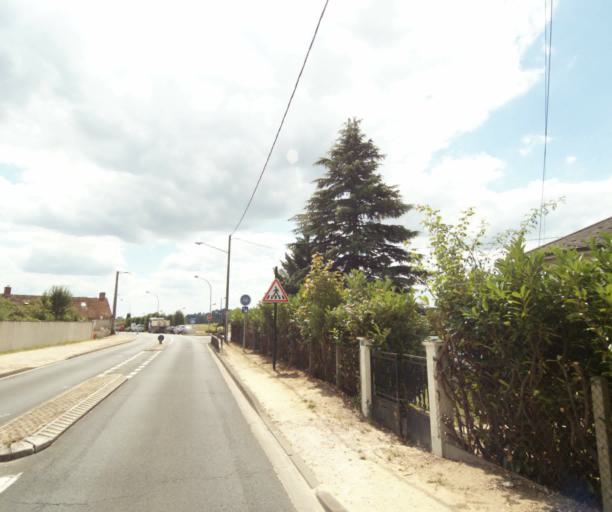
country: FR
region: Centre
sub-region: Departement du Loiret
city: Saint-Cyr-en-Val
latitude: 47.8363
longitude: 1.9580
